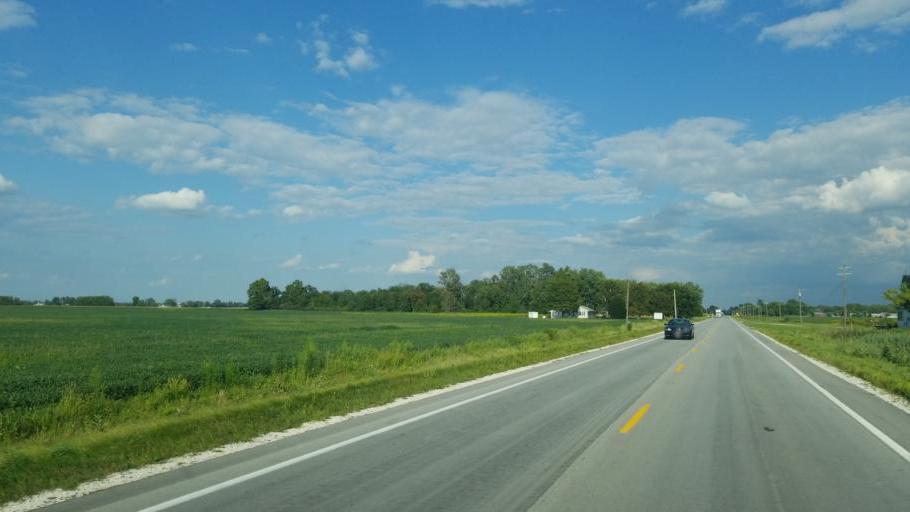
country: US
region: Ohio
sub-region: Sandusky County
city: Stony Prairie
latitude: 41.3417
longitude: -83.2125
